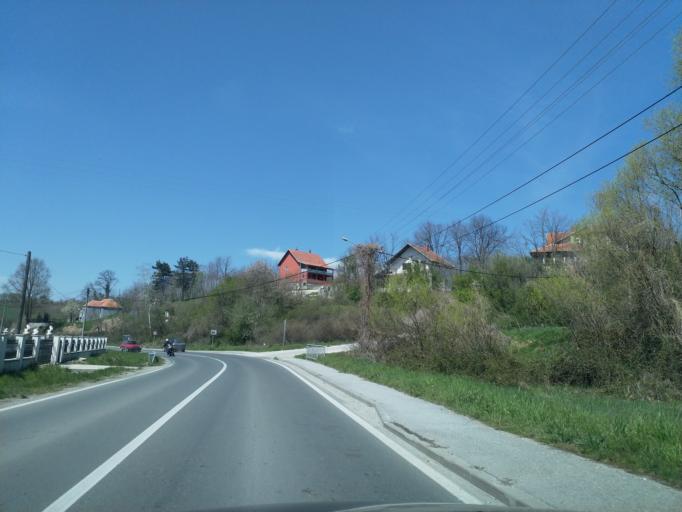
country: RS
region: Central Serbia
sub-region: Sumadijski Okrug
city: Arangelovac
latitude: 44.3343
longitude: 20.4988
